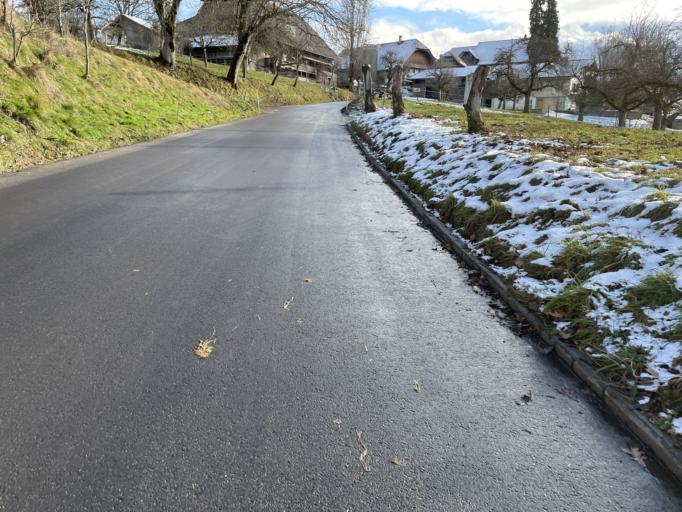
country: CH
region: Lucerne
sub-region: Entlebuch District
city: Oberdiessbach
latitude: 46.8591
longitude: 7.6033
